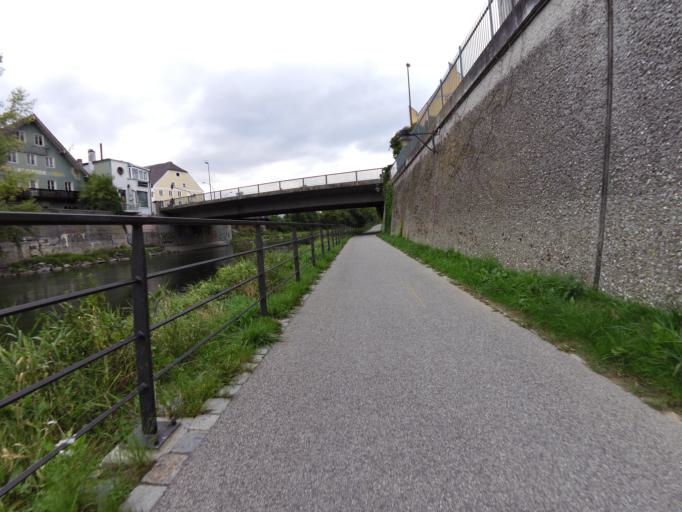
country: DE
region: Bavaria
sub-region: Lower Bavaria
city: Landshut
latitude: 48.5406
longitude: 12.1497
